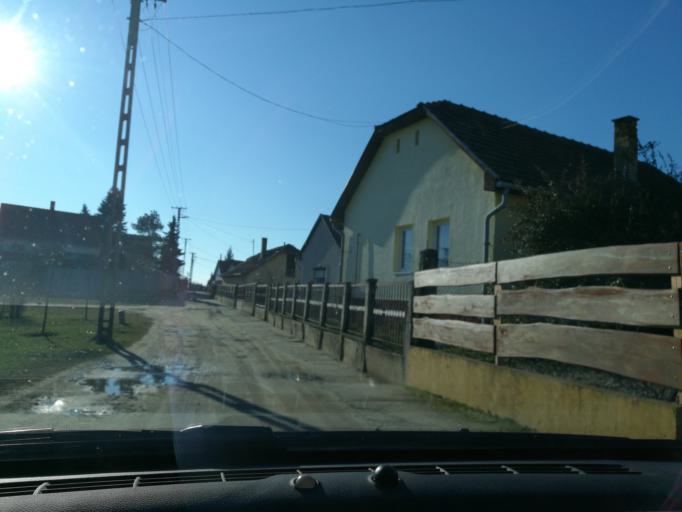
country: HU
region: Szabolcs-Szatmar-Bereg
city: Nyiregyhaza
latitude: 47.9253
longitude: 21.7581
